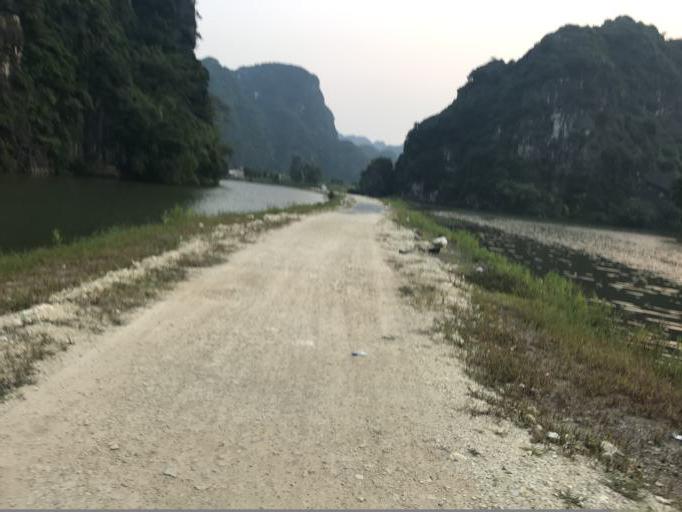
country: VN
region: Ninh Binh
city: Thi Tran Thien Ton
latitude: 20.2548
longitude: 105.9282
